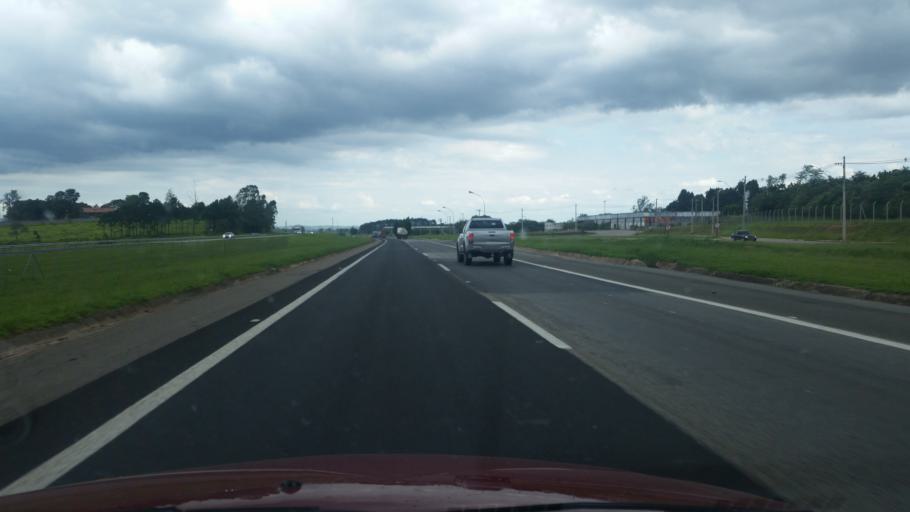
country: BR
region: Sao Paulo
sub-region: Sorocaba
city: Sorocaba
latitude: -23.3695
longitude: -47.4590
